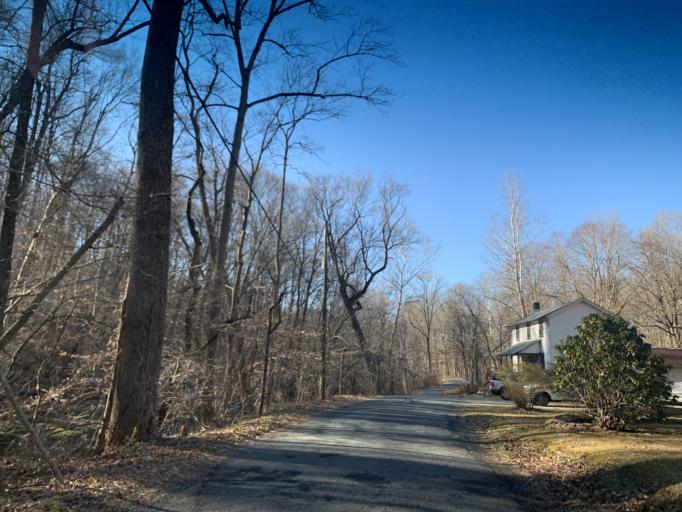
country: US
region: Maryland
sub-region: Cecil County
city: Rising Sun
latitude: 39.6559
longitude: -76.1412
